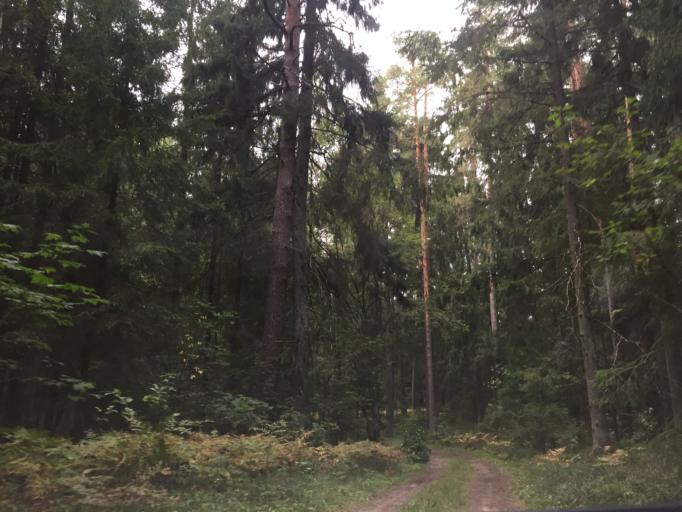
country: LV
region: Baldone
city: Baldone
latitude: 56.7723
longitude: 24.4523
